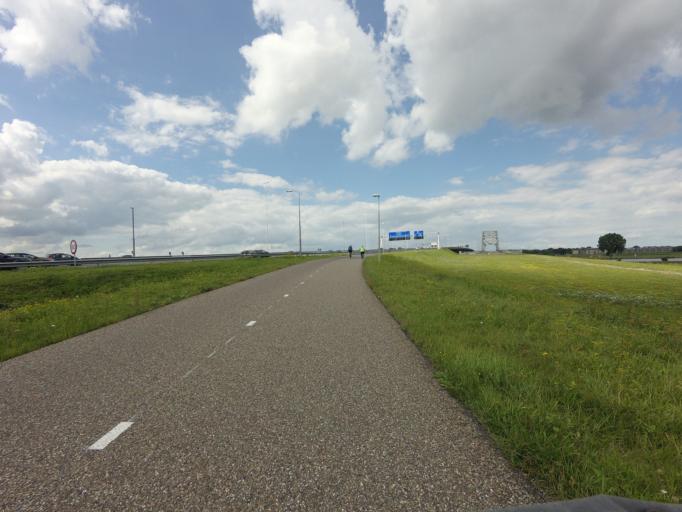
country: NL
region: Utrecht
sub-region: Gemeente Vianen
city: Vianen
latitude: 51.9939
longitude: 5.0807
